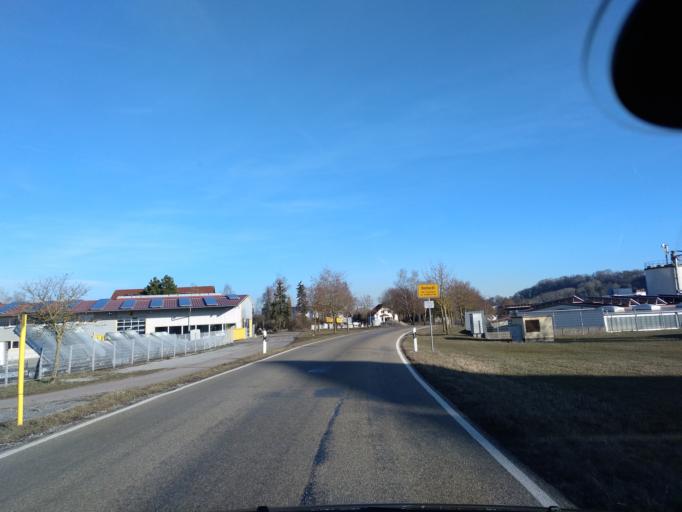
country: DE
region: Baden-Wuerttemberg
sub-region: Regierungsbezirk Stuttgart
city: Rosenberg
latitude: 49.0717
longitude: 10.0270
